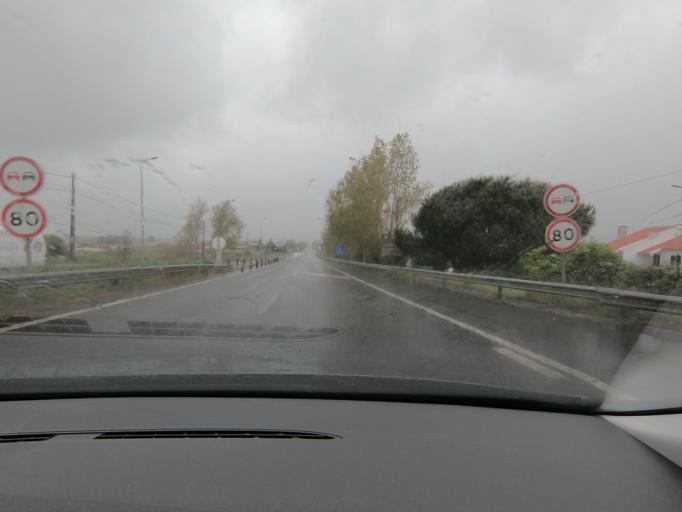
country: PT
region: Lisbon
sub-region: Sintra
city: Sintra
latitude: 38.8205
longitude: -9.3590
